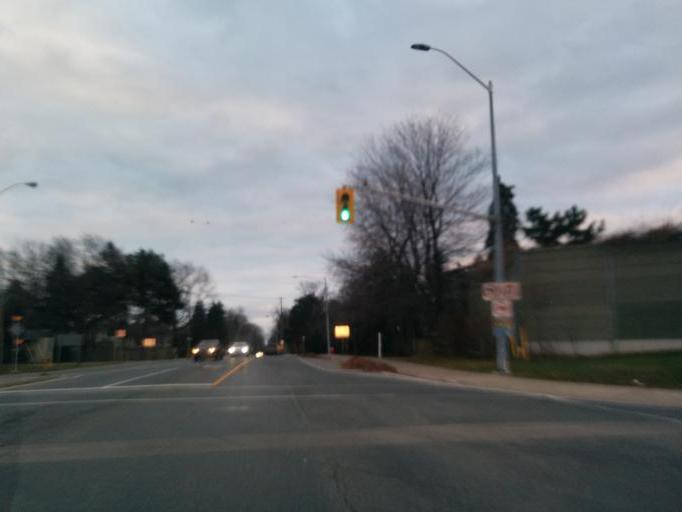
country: CA
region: Ontario
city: Mississauga
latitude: 43.5522
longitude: -79.6122
